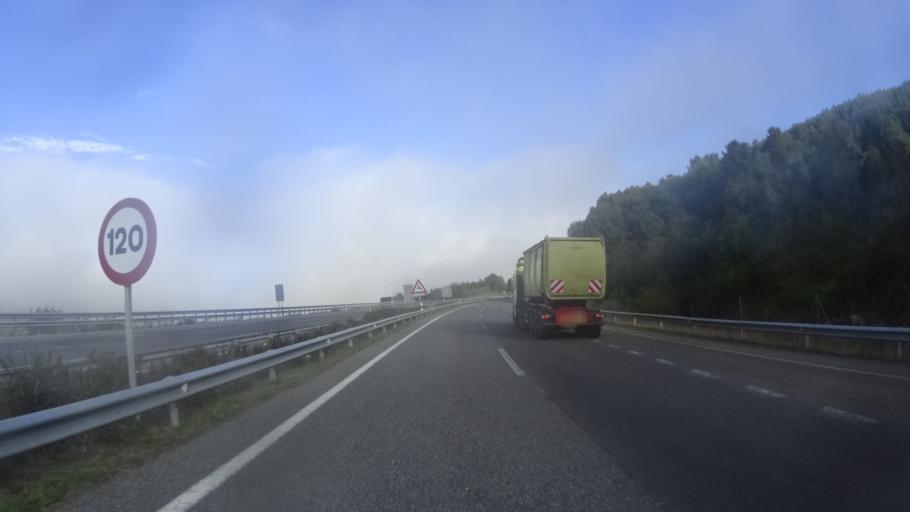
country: ES
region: Galicia
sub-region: Provincia de Lugo
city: Becerrea
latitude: 42.8887
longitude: -7.1814
